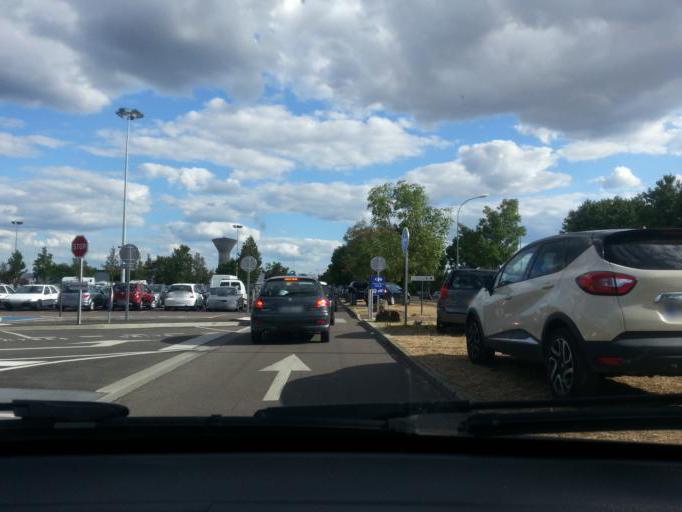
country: FR
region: Bourgogne
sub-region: Departement de Saone-et-Loire
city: Chalon-sur-Saone
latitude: 46.7747
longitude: 4.8585
